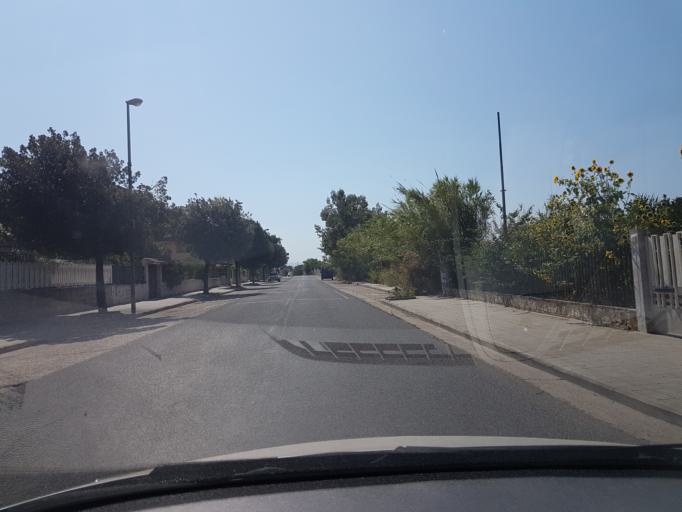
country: IT
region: Sardinia
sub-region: Provincia di Oristano
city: Solanas
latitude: 39.9288
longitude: 8.5537
